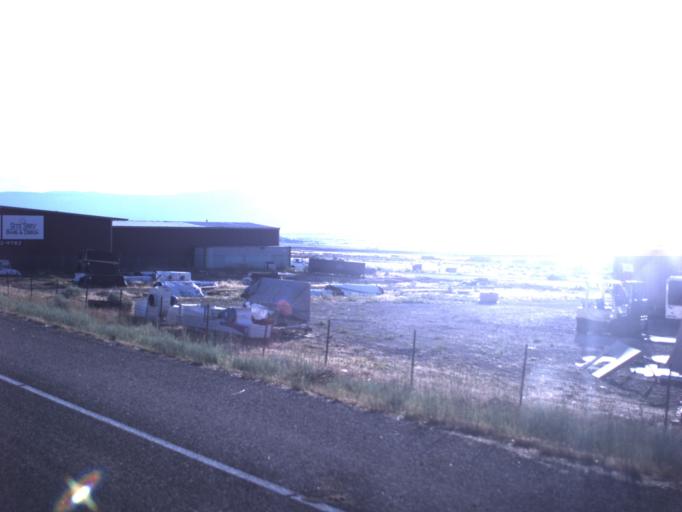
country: US
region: Utah
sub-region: Sanpete County
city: Mount Pleasant
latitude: 39.5274
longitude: -111.4703
